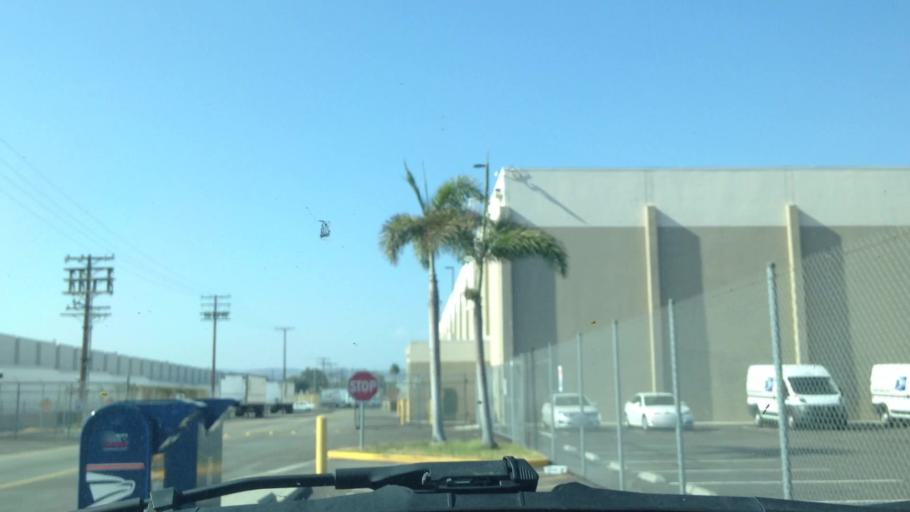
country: US
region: California
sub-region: Orange County
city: Yorba Linda
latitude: 33.8598
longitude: -117.8022
